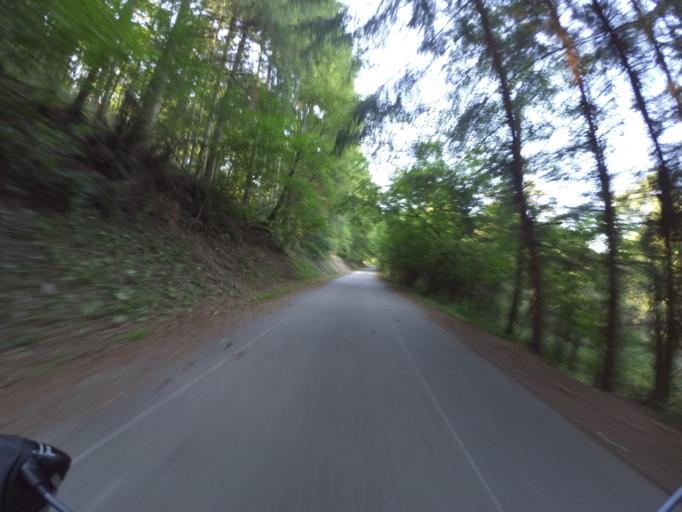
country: DE
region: Rheinland-Pfalz
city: Thornich
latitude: 49.8527
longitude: 6.8368
